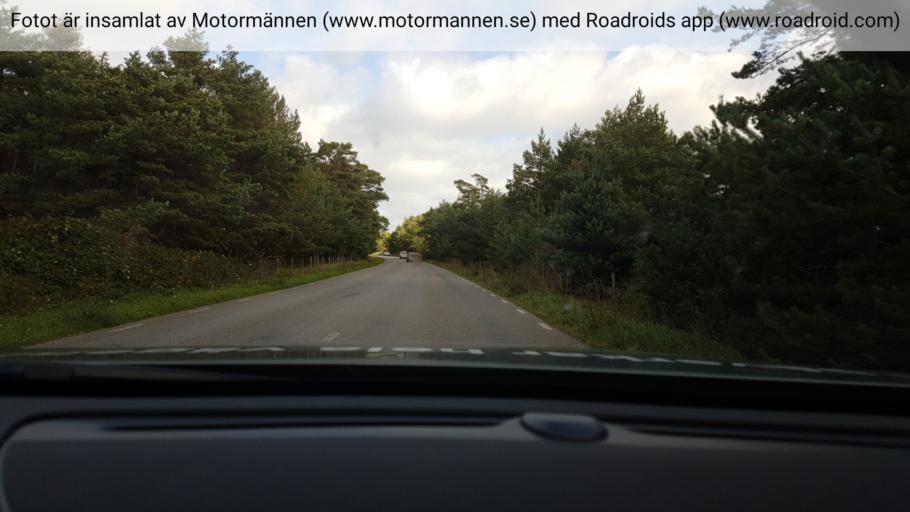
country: SE
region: Gotland
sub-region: Gotland
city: Slite
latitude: 57.9407
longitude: 19.2021
